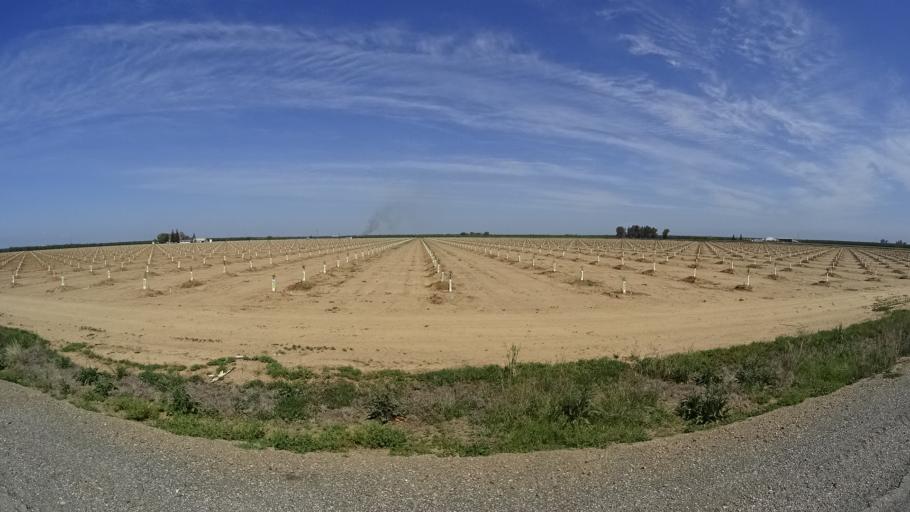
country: US
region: California
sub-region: Glenn County
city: Orland
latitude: 39.6527
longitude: -122.1091
